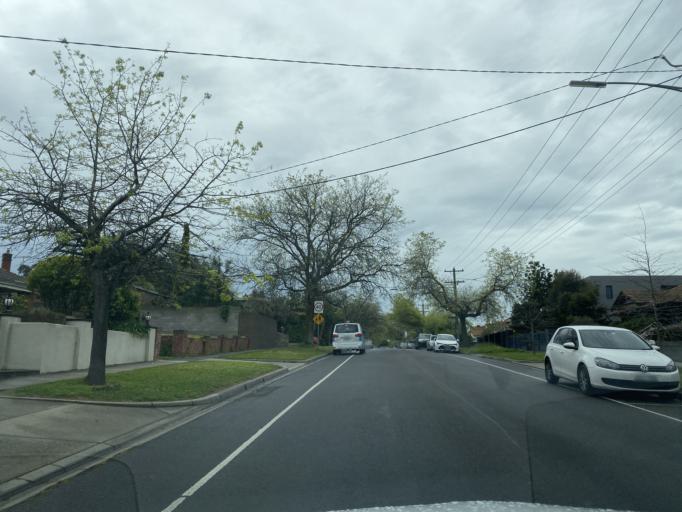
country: AU
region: Victoria
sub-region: Boroondara
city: Camberwell
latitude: -37.8402
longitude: 145.0839
